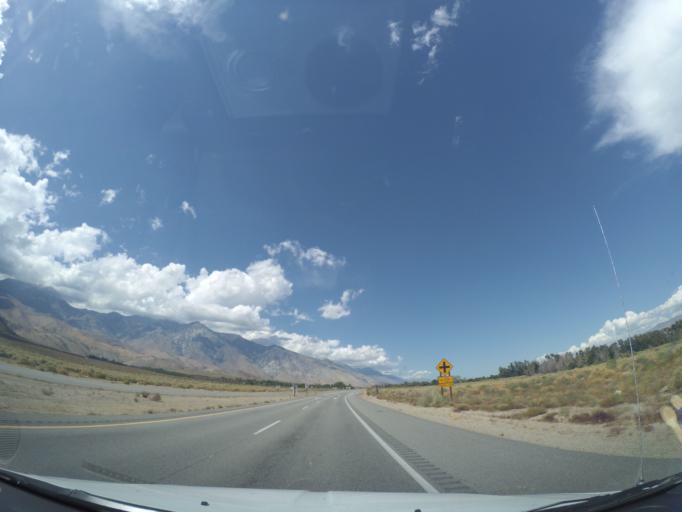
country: US
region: California
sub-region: Inyo County
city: Lone Pine
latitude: 36.8280
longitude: -118.2215
